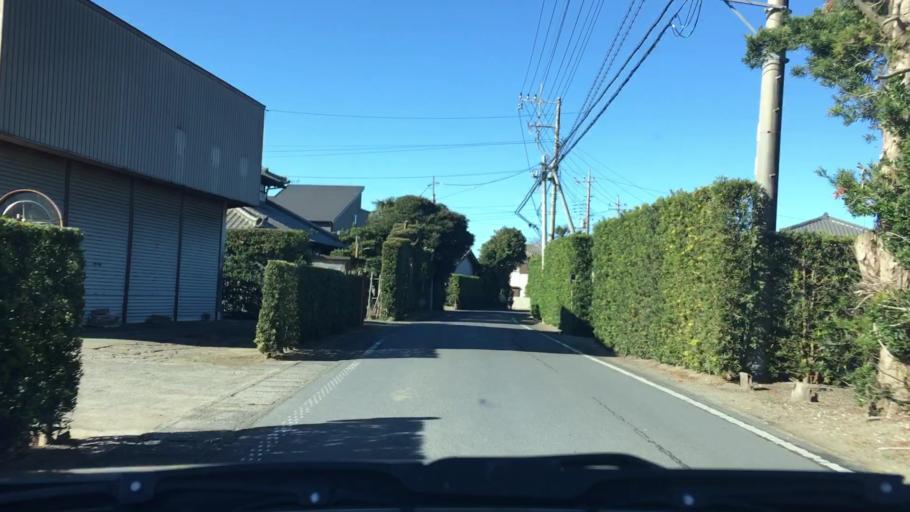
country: JP
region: Chiba
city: Omigawa
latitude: 35.8696
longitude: 140.6426
